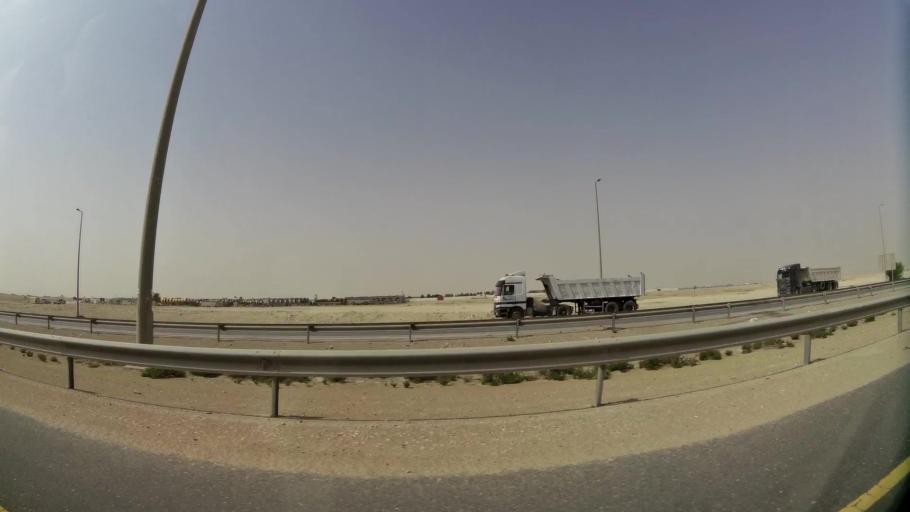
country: QA
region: Baladiyat ar Rayyan
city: Ar Rayyan
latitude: 25.1626
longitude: 51.3001
